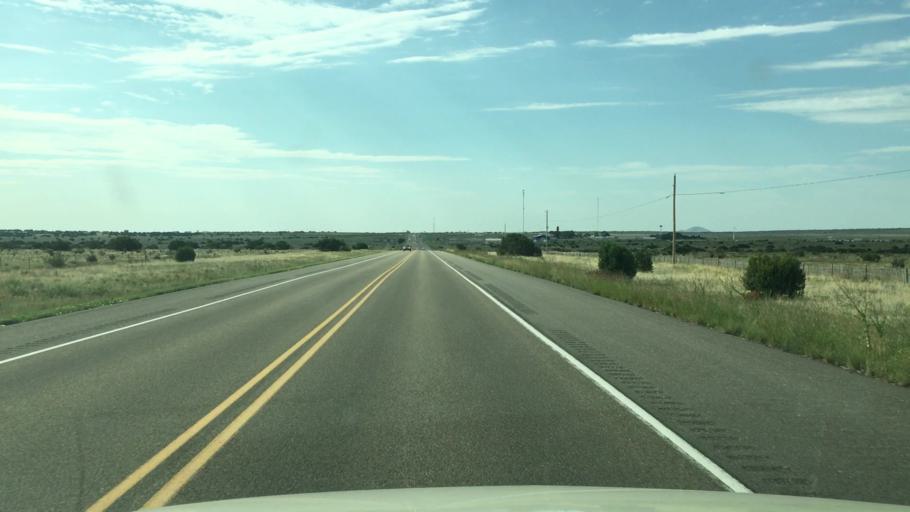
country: US
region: New Mexico
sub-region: Torrance County
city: Moriarty
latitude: 35.0252
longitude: -105.6737
